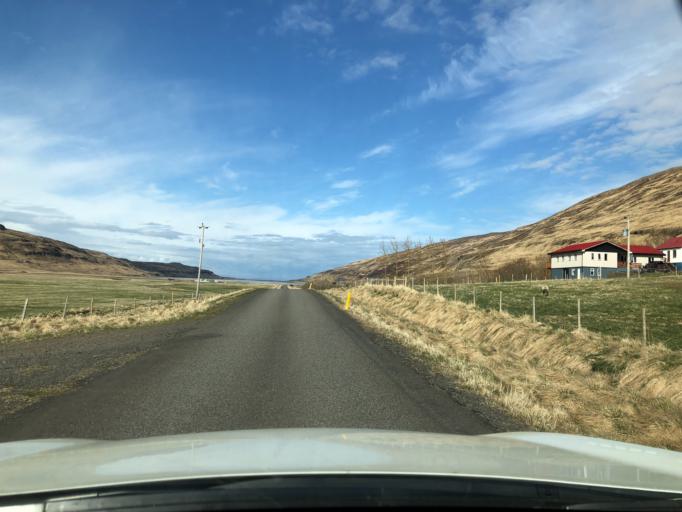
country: IS
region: West
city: Borgarnes
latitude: 65.0580
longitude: -21.5469
